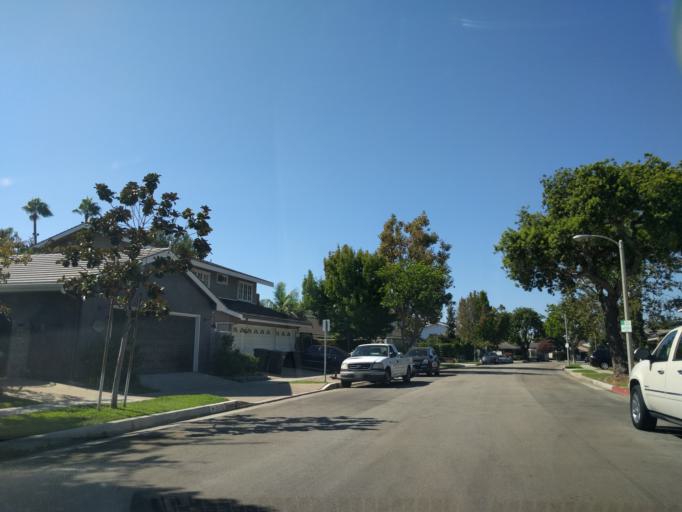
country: US
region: California
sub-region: Orange County
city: San Joaquin Hills
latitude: 33.6320
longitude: -117.8745
